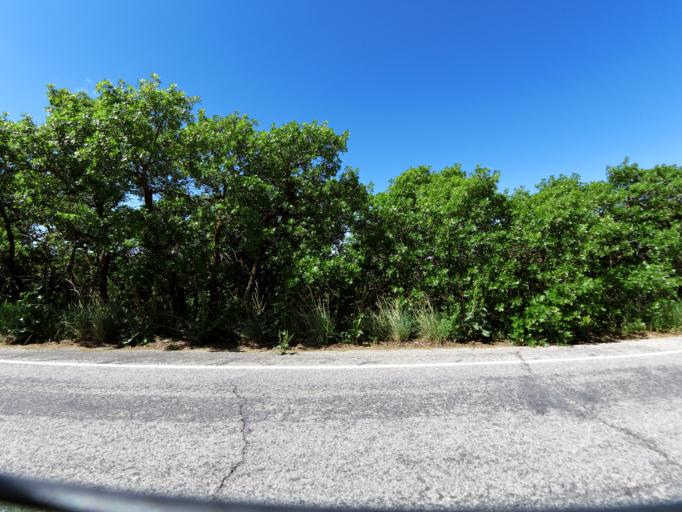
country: US
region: Utah
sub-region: Weber County
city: Washington Terrace
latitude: 41.1712
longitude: -111.9434
